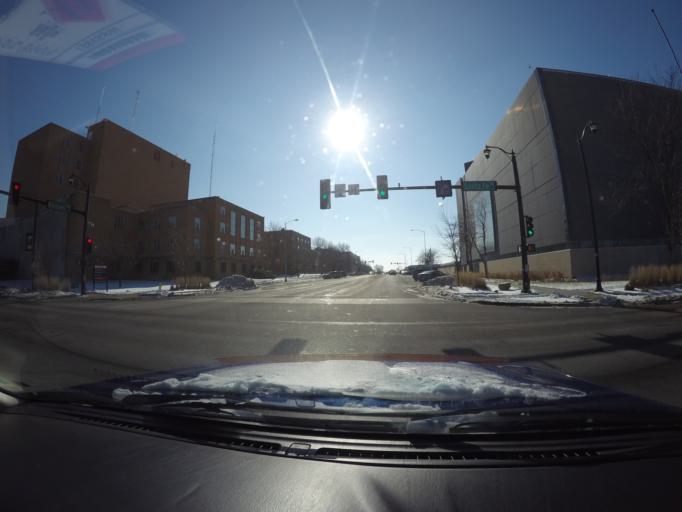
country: US
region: Kansas
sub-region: Johnson County
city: Olathe
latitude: 38.8836
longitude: -94.8207
